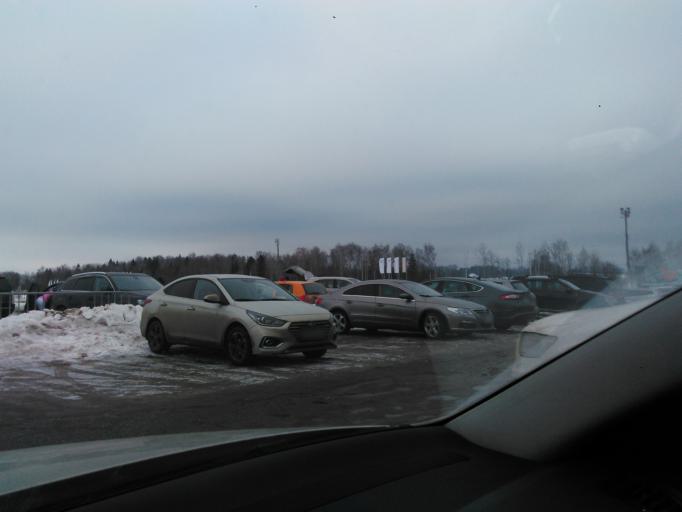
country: RU
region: Moskovskaya
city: Dedenevo
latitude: 56.2790
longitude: 37.5653
